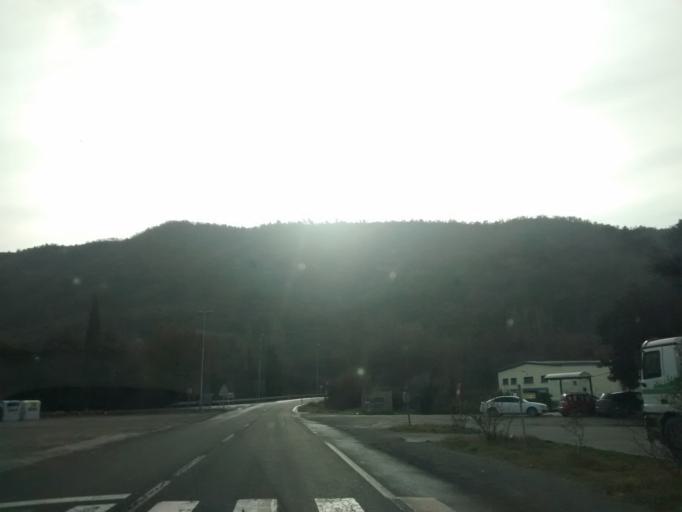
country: ES
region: Aragon
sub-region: Provincia de Huesca
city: Bailo
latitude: 42.5568
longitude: -0.7865
